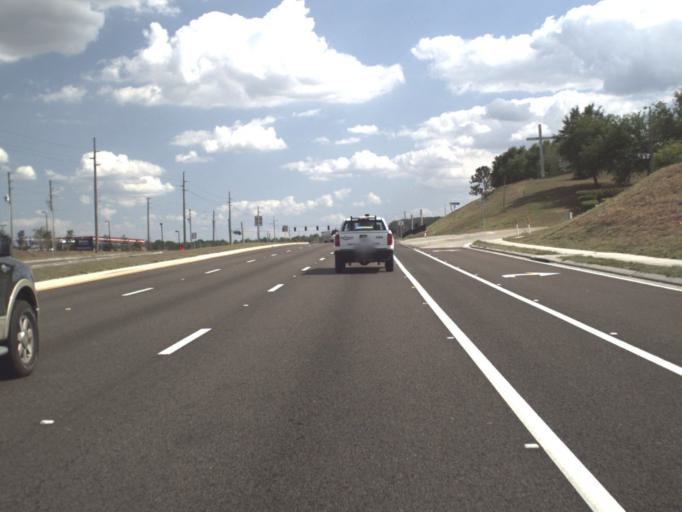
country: US
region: Florida
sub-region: Lake County
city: Clermont
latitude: 28.5224
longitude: -81.7299
